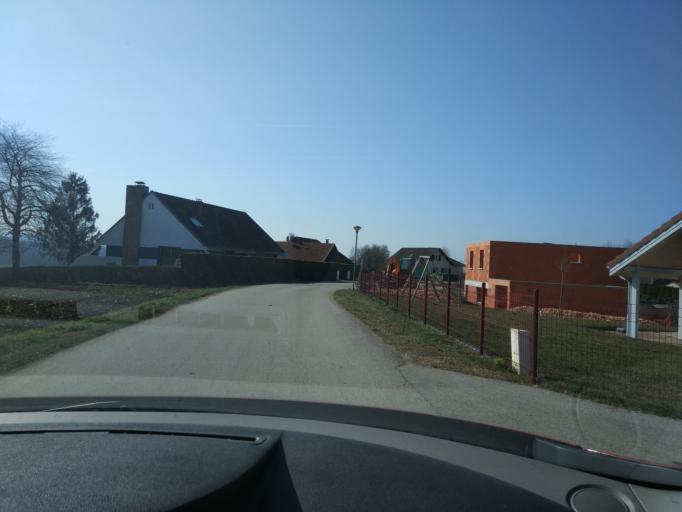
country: FR
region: Franche-Comte
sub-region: Departement du Doubs
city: Saone
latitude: 47.2185
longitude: 6.1251
